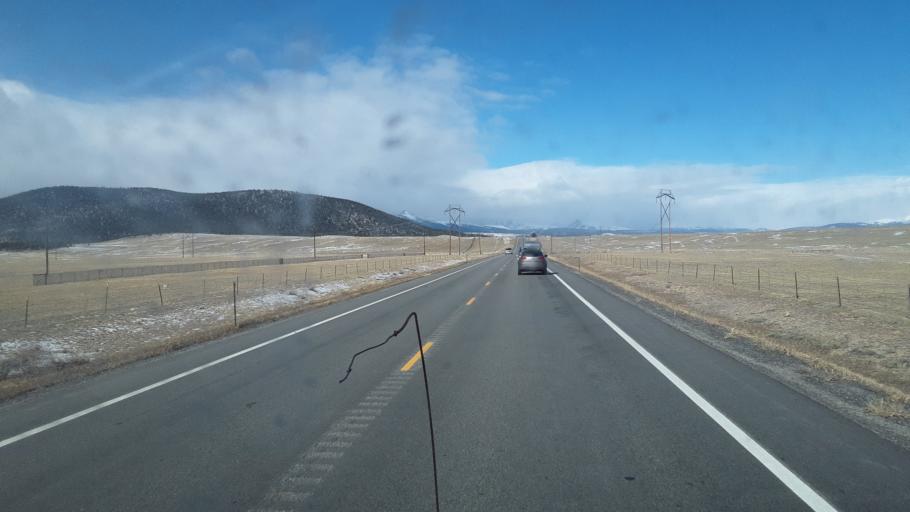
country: US
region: Colorado
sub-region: Park County
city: Fairplay
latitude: 39.0823
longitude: -105.9762
